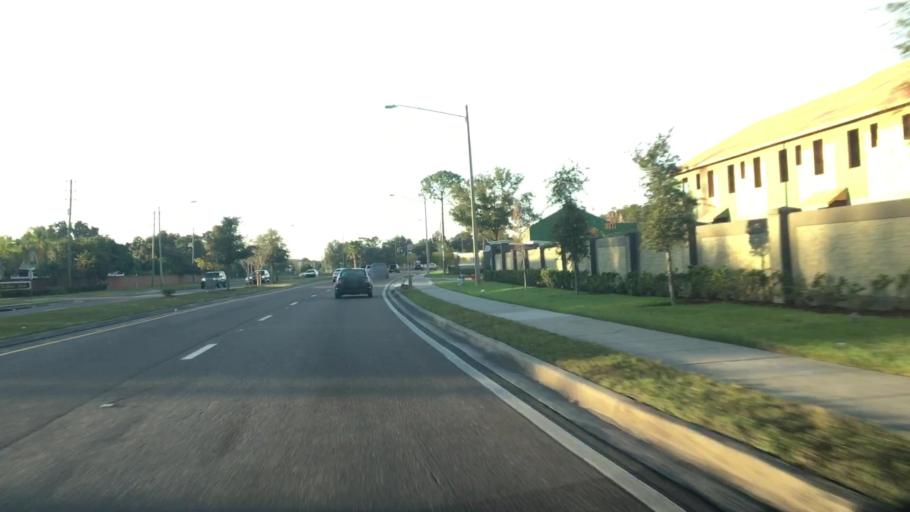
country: US
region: Florida
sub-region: Orange County
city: Conway
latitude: 28.4847
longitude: -81.2855
